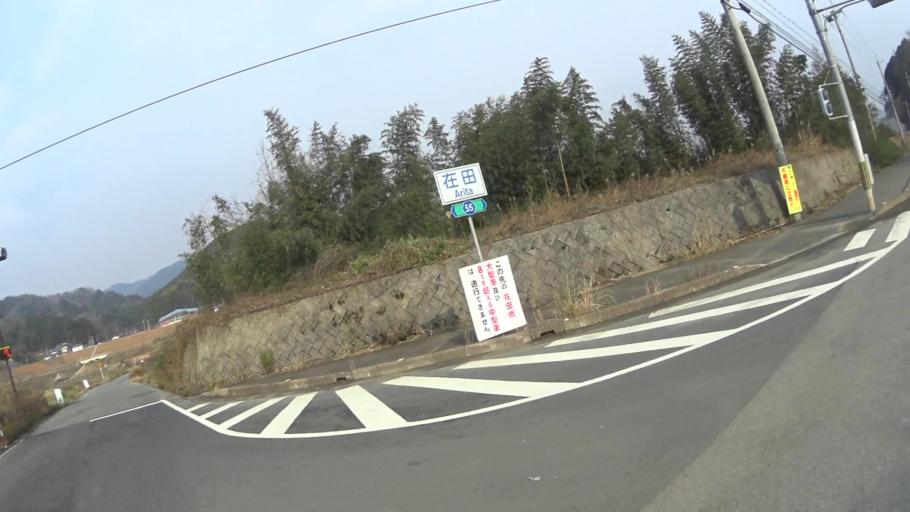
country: JP
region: Kyoto
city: Fukuchiyama
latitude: 35.3682
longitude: 135.1305
